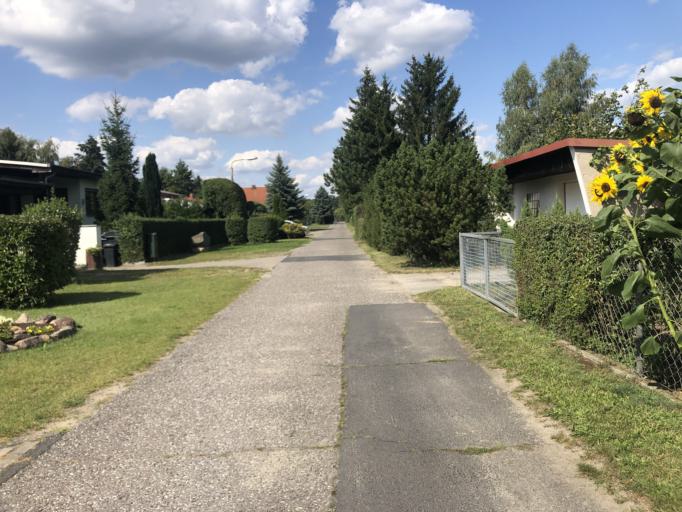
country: DE
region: Brandenburg
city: Mullrose
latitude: 52.2338
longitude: 14.4122
